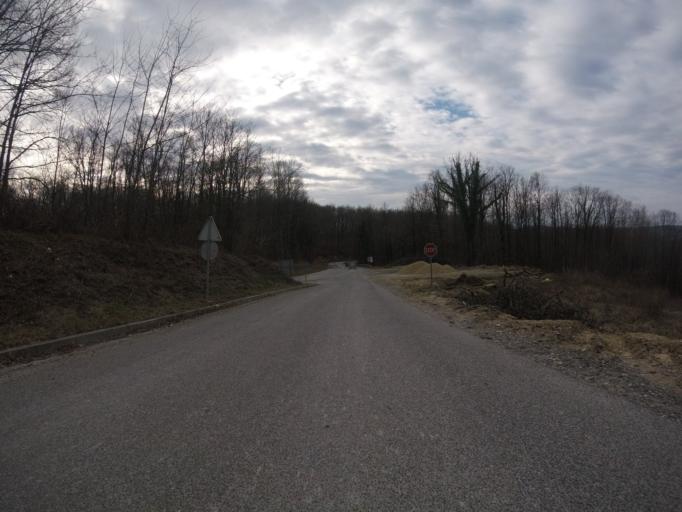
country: HR
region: Sisacko-Moslavacka
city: Glina
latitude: 45.4877
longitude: 16.0459
